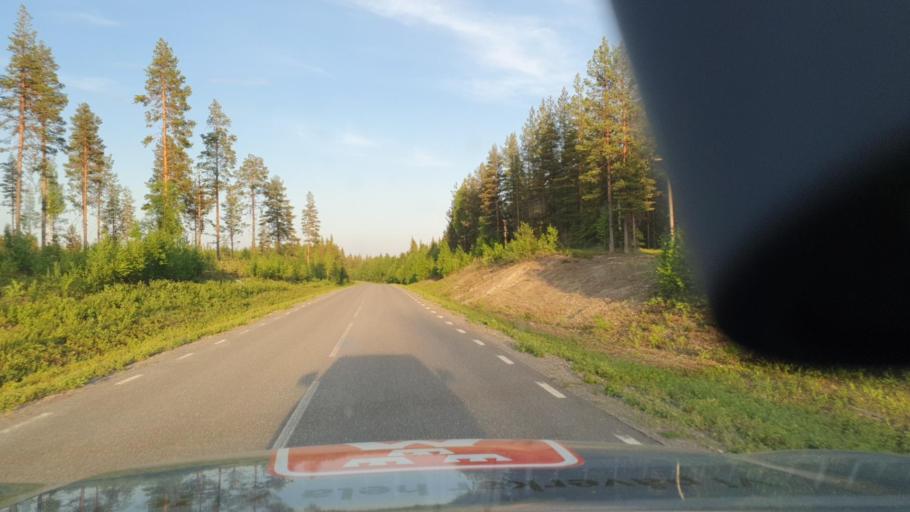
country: SE
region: Norrbotten
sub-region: Bodens Kommun
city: Boden
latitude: 66.2138
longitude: 21.4377
